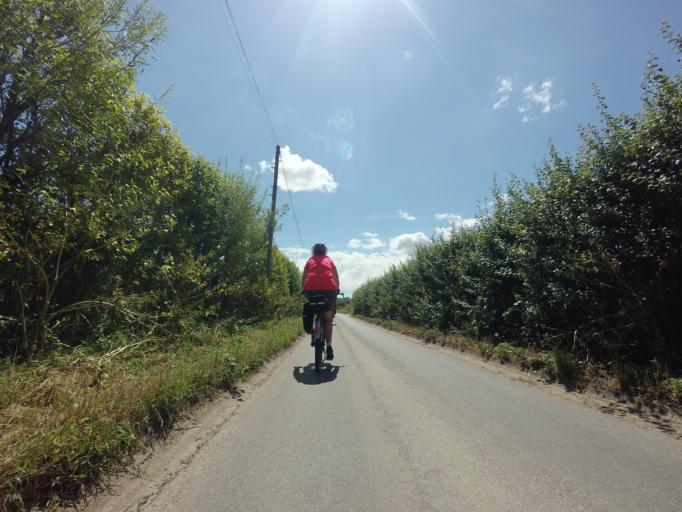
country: GB
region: England
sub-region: Medway
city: Cooling
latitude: 51.4554
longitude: 0.5112
